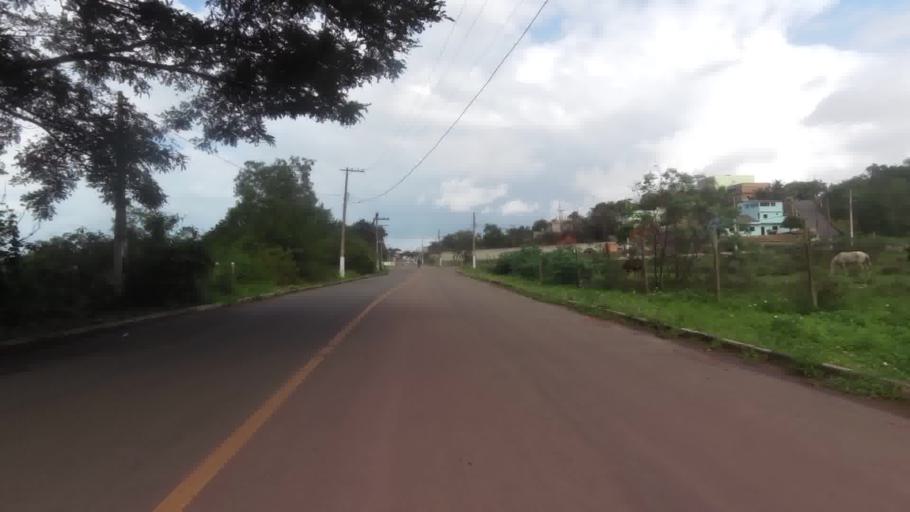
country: BR
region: Espirito Santo
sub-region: Piuma
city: Piuma
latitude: -20.7966
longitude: -40.6396
